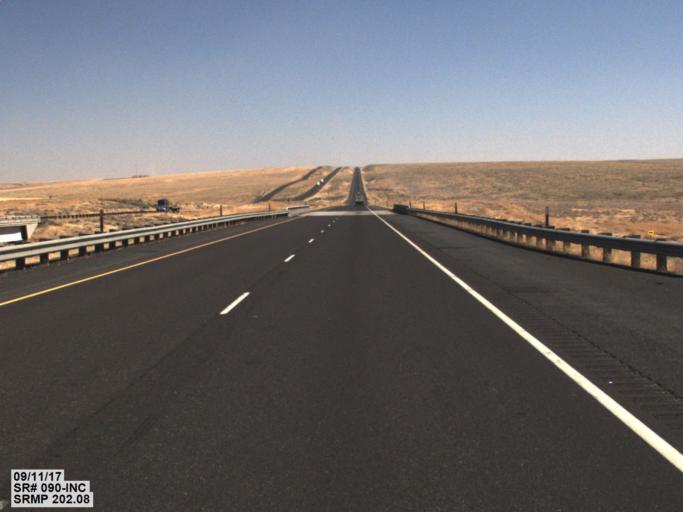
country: US
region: Washington
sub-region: Grant County
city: Warden
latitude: 47.0860
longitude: -118.7657
